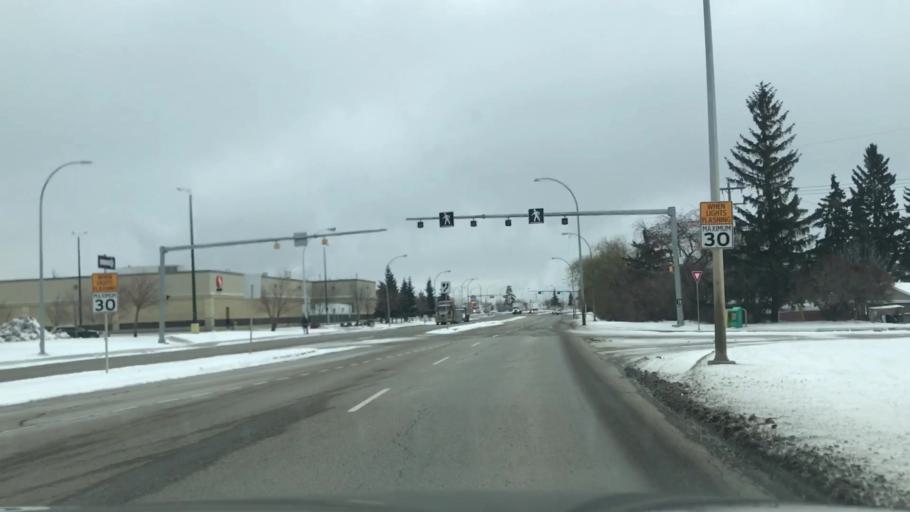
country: CA
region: Alberta
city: Edmonton
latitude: 53.5383
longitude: -113.4273
